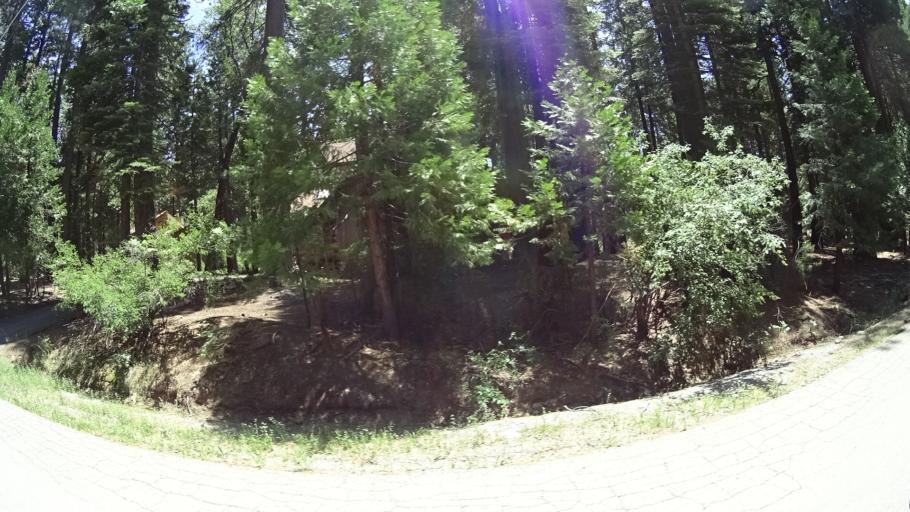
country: US
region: California
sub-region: Calaveras County
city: Arnold
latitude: 38.3022
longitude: -120.2637
